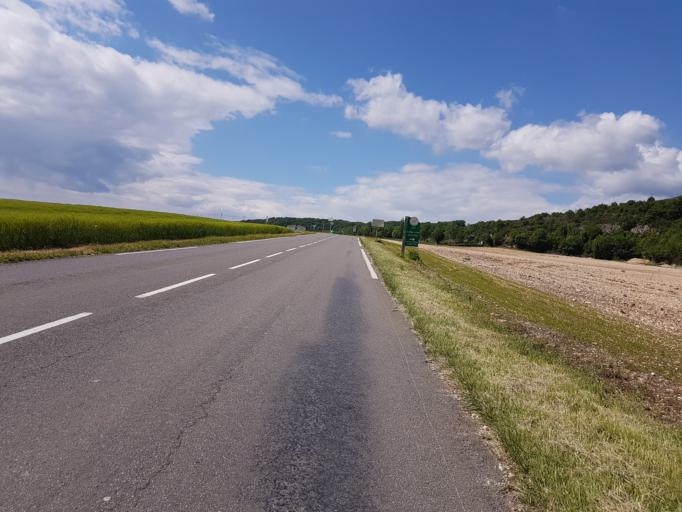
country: FR
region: Rhone-Alpes
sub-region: Departement de l'Isere
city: Creys-Mepieu
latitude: 45.7188
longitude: 5.5417
